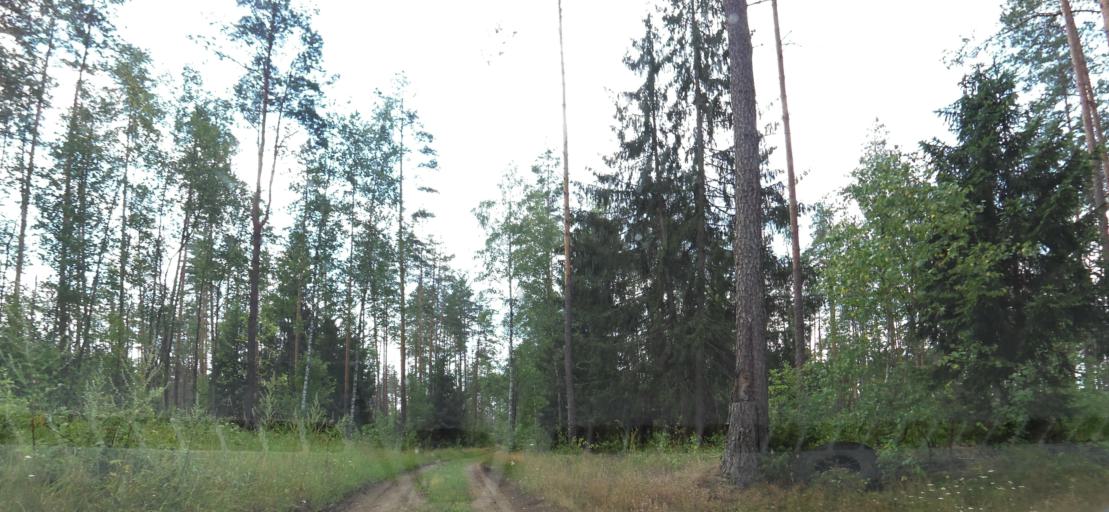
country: LT
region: Alytaus apskritis
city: Varena
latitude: 54.2425
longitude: 24.6543
